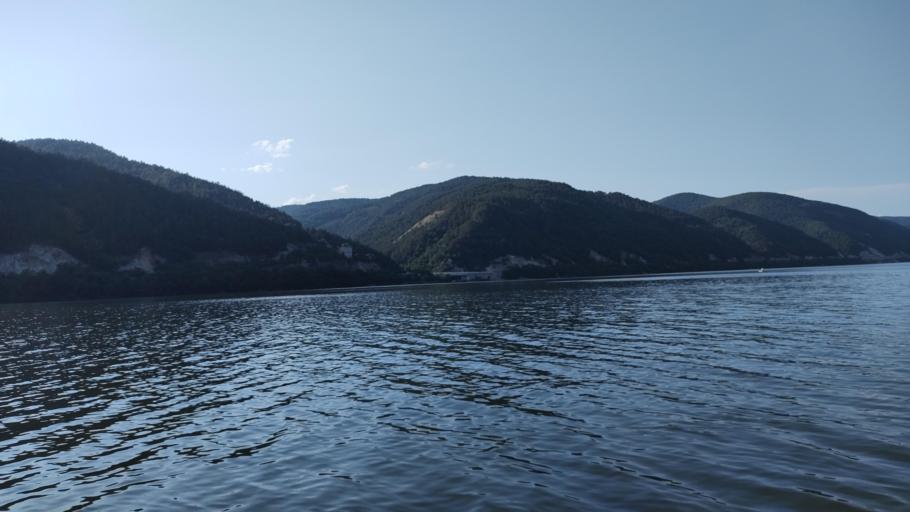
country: RO
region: Mehedinti
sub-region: Comuna Svinita
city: Svinita
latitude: 44.5235
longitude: 22.2072
